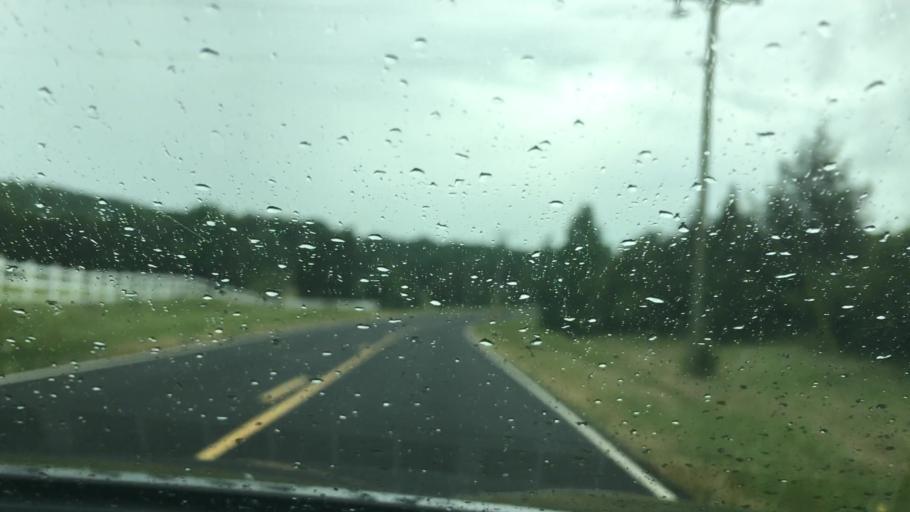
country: US
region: North Carolina
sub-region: Stanly County
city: Badin
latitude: 35.3672
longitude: -80.1159
